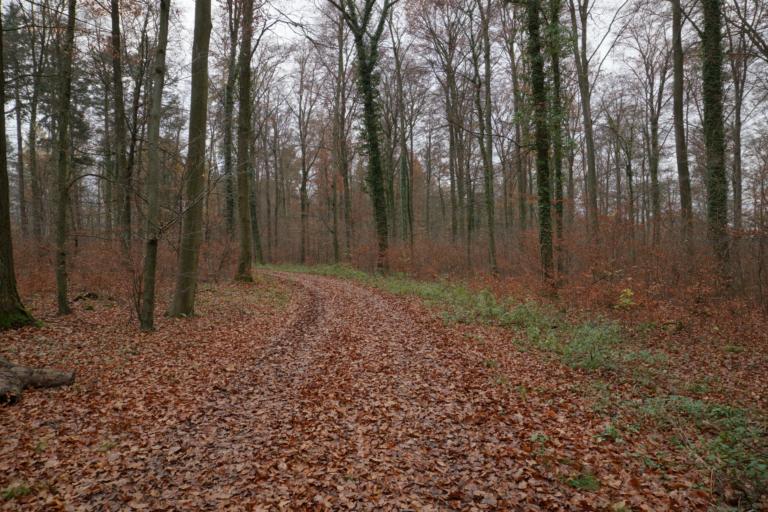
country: DE
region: Baden-Wuerttemberg
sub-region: Karlsruhe Region
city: Huffenhardt
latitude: 49.3066
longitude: 9.0442
